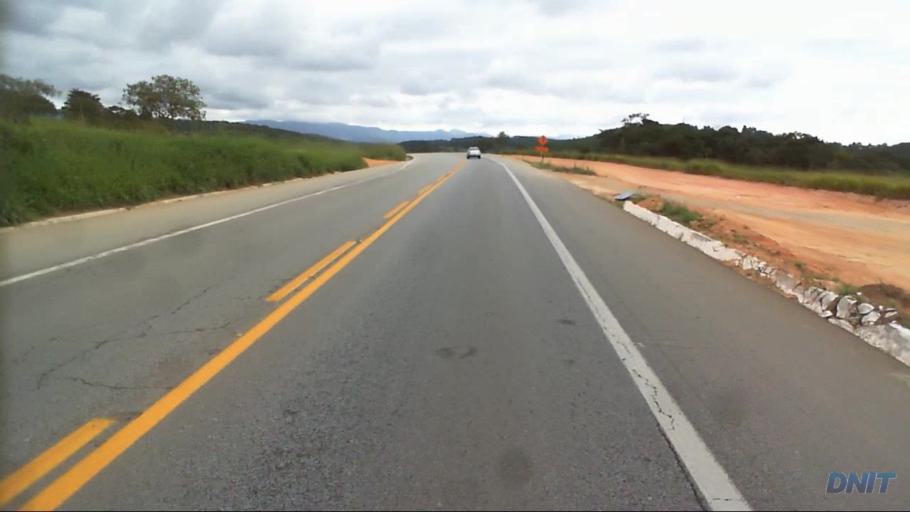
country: BR
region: Minas Gerais
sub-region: Barao De Cocais
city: Barao de Cocais
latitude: -19.7631
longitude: -43.4599
